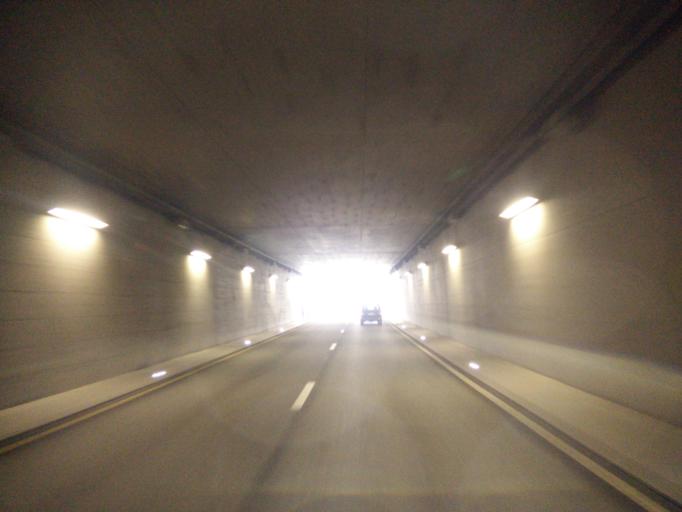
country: NO
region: Nord-Trondelag
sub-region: Stjordal
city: Stjordal
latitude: 63.4715
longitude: 10.9079
